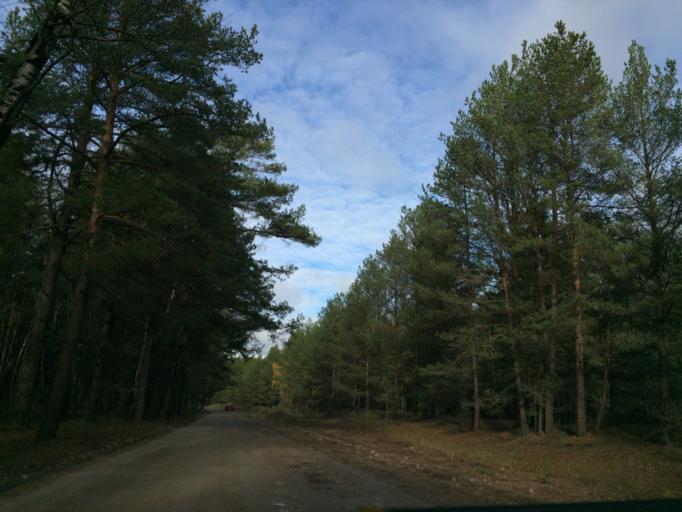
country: LV
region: Carnikava
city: Carnikava
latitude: 57.1374
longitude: 24.2663
